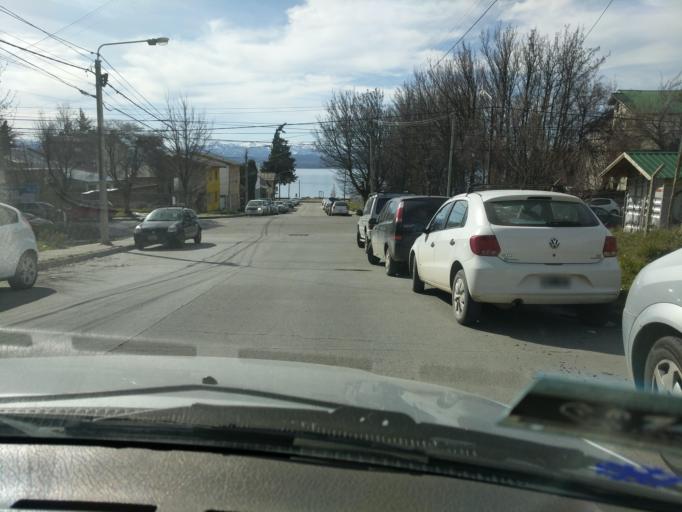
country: AR
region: Rio Negro
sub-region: Departamento de Bariloche
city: San Carlos de Bariloche
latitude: -41.1344
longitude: -71.2940
